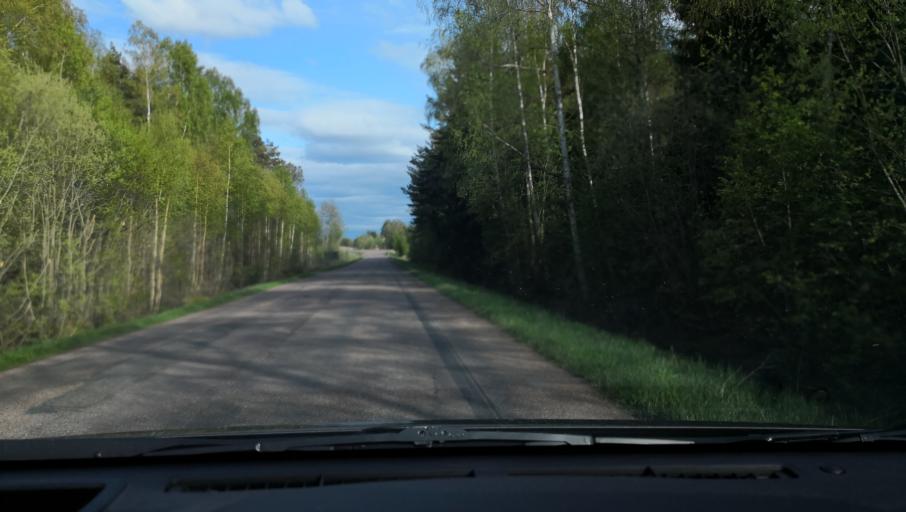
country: SE
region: Dalarna
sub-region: Saters Kommun
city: Saeter
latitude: 60.2989
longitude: 15.8545
